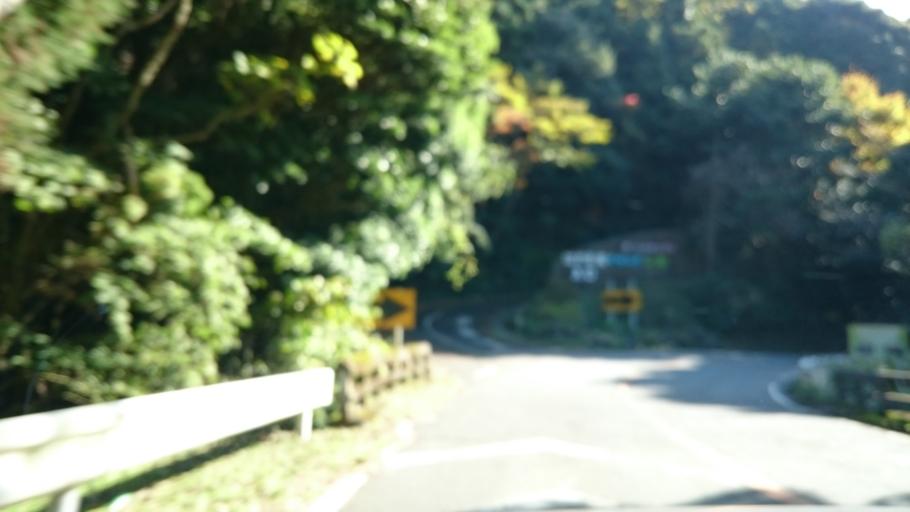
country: JP
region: Shizuoka
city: Heda
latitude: 34.9681
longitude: 138.8146
